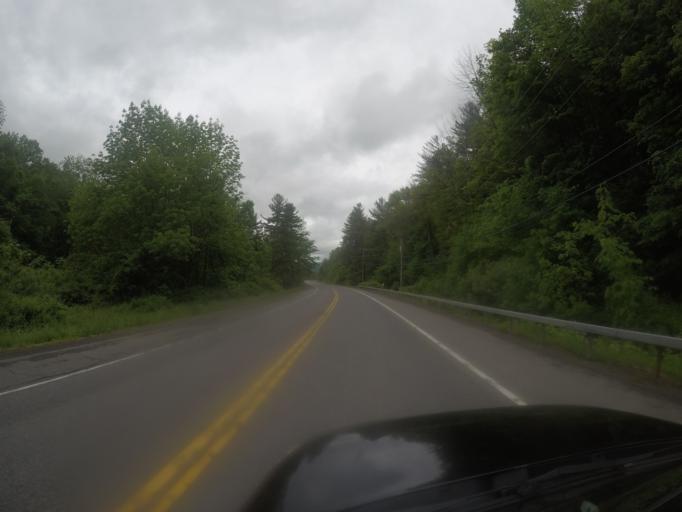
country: US
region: New York
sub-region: Ulster County
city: Shokan
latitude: 42.0931
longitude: -74.3343
